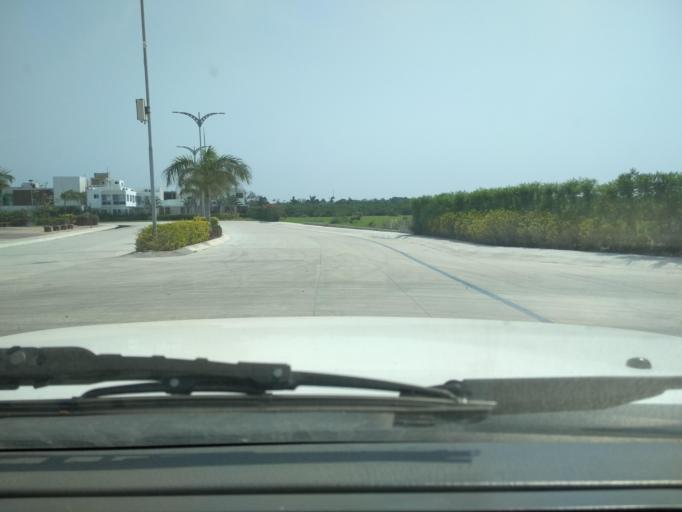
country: MX
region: Veracruz
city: Boca del Rio
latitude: 19.1059
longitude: -96.1262
